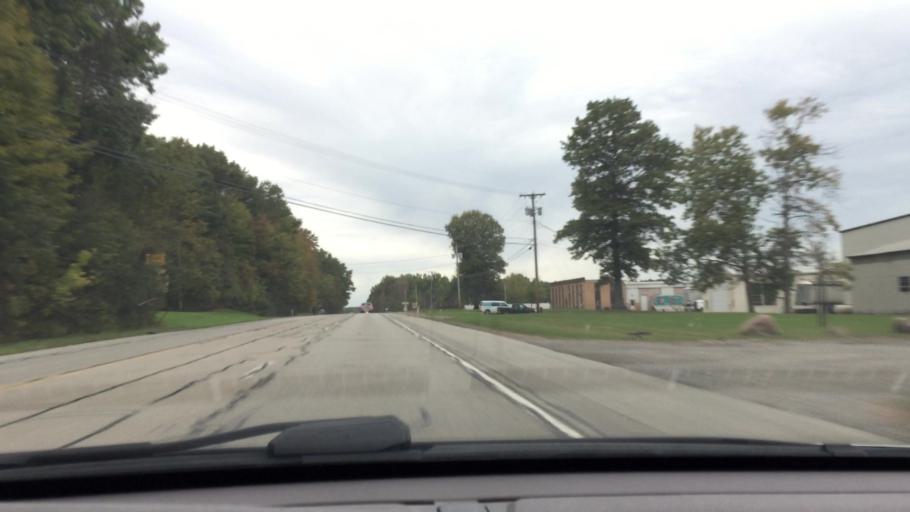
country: US
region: Pennsylvania
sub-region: Lawrence County
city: Oakwood
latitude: 41.0598
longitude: -80.4518
